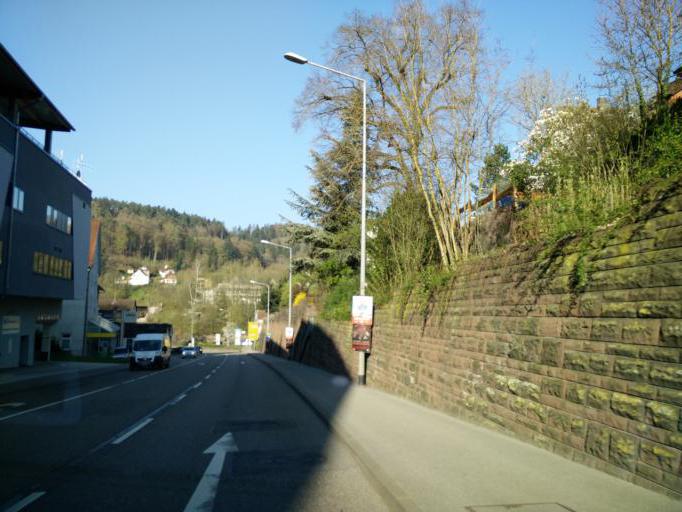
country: DE
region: Baden-Wuerttemberg
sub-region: Karlsruhe Region
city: Calw
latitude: 48.7137
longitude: 8.7459
